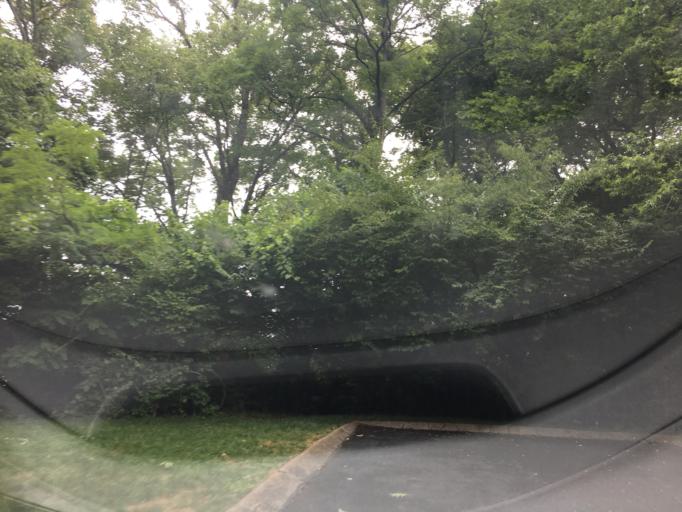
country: US
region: Tennessee
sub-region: Davidson County
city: Belle Meade
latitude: 36.0964
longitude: -86.8285
